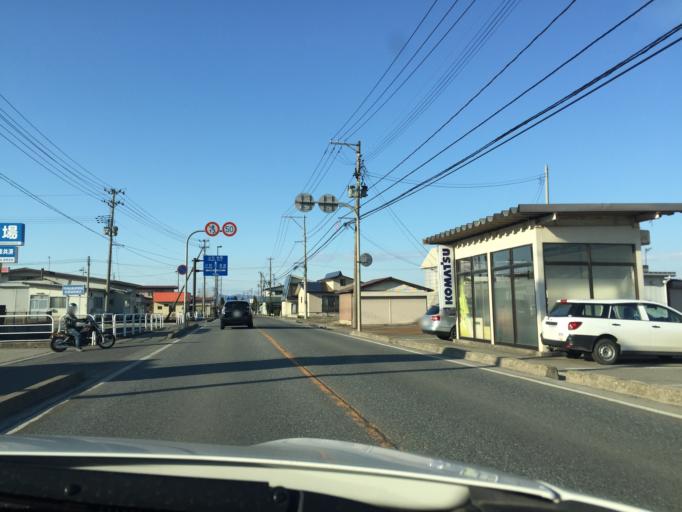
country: JP
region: Yamagata
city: Yonezawa
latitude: 37.9527
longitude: 140.1241
